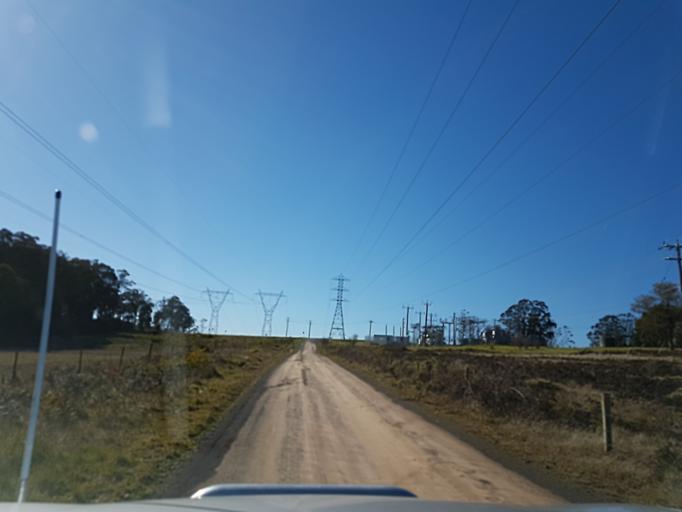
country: AU
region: Victoria
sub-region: Murrindindi
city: Kinglake West
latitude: -37.5150
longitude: 145.3146
